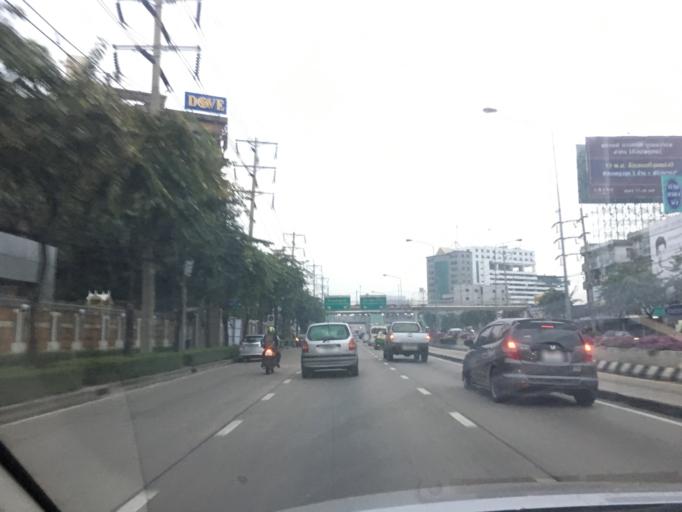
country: TH
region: Bangkok
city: Bang Kho Laem
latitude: 13.6920
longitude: 100.5017
